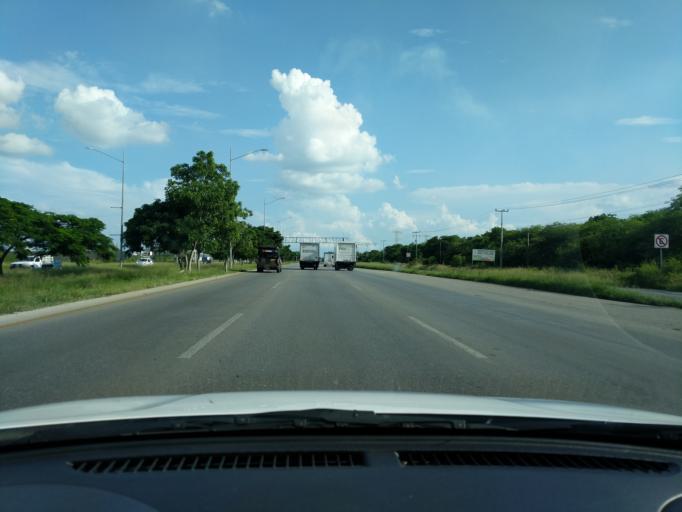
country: MX
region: Yucatan
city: Itzincab Palomeque
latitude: 20.9447
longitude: -89.7001
